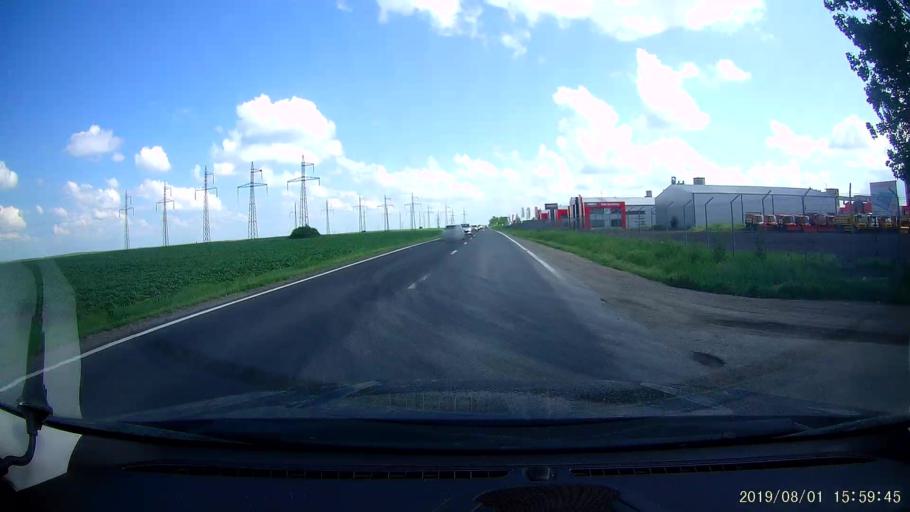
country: RO
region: Ialomita
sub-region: Comuna Slobozia
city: Slobozia
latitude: 44.5418
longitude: 27.3854
